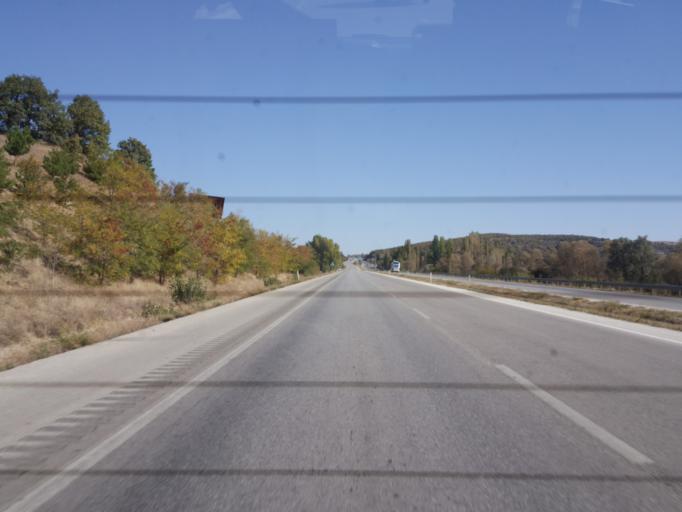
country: TR
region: Corum
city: Alaca
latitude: 40.2675
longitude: 34.6372
